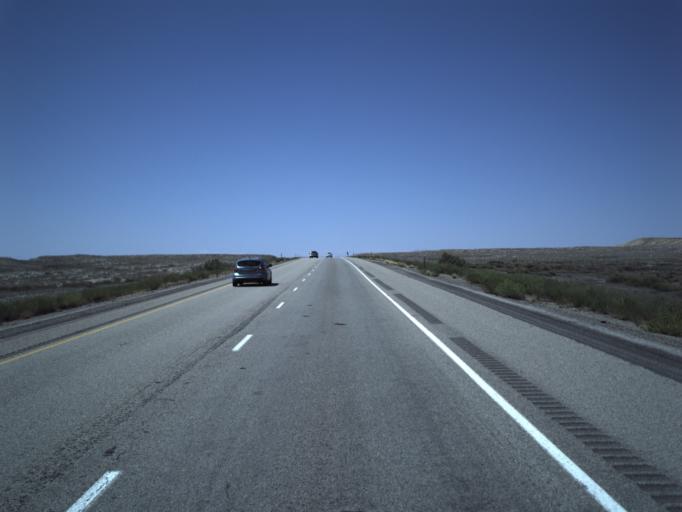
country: US
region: Utah
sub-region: Grand County
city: Moab
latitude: 38.9732
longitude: -109.3604
